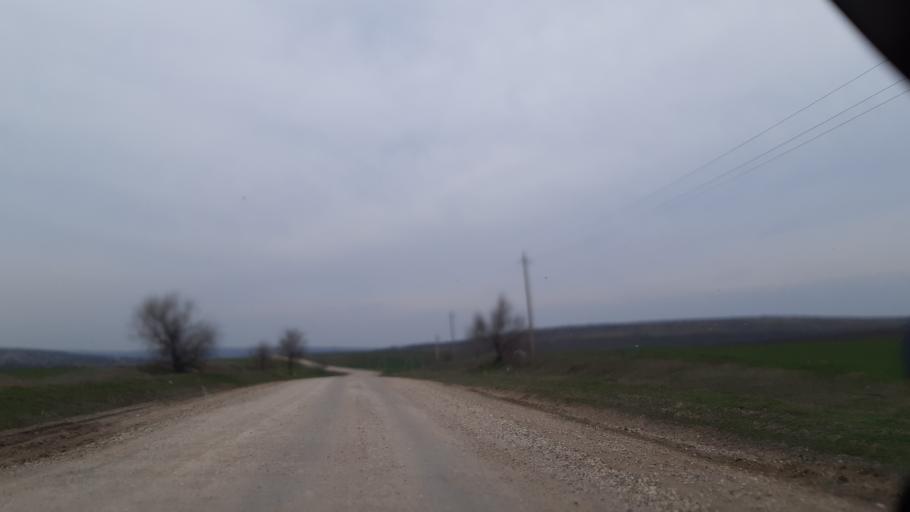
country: MD
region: Soldanesti
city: Soldanesti
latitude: 47.6188
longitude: 28.6574
